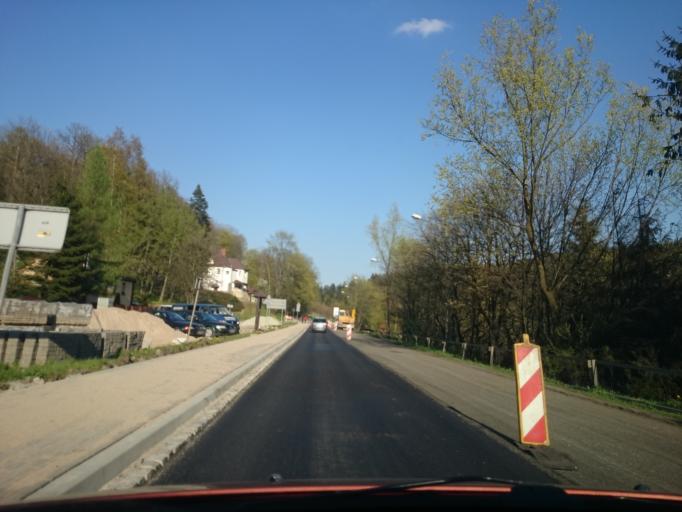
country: PL
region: Lower Silesian Voivodeship
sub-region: Powiat klodzki
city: Duszniki-Zdroj
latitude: 50.4047
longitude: 16.3975
